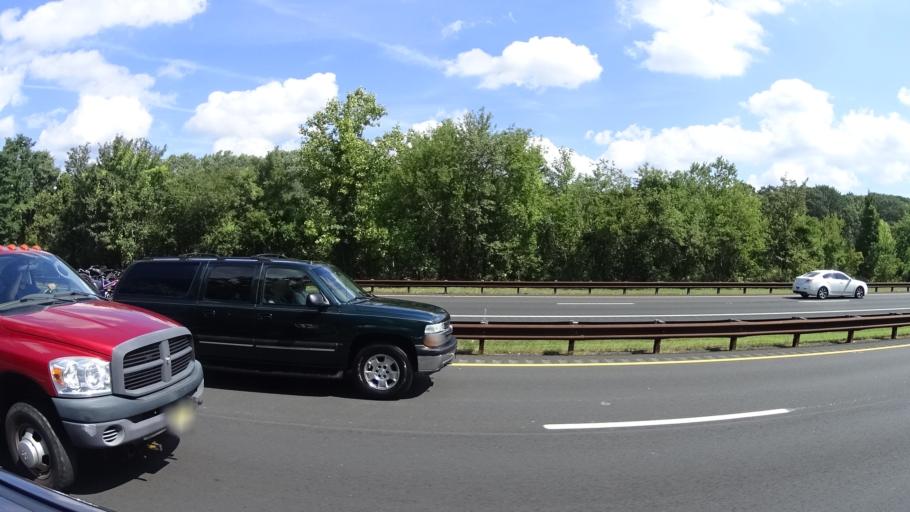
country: US
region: New Jersey
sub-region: Monmouth County
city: Lincroft
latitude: 40.3786
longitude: -74.1543
